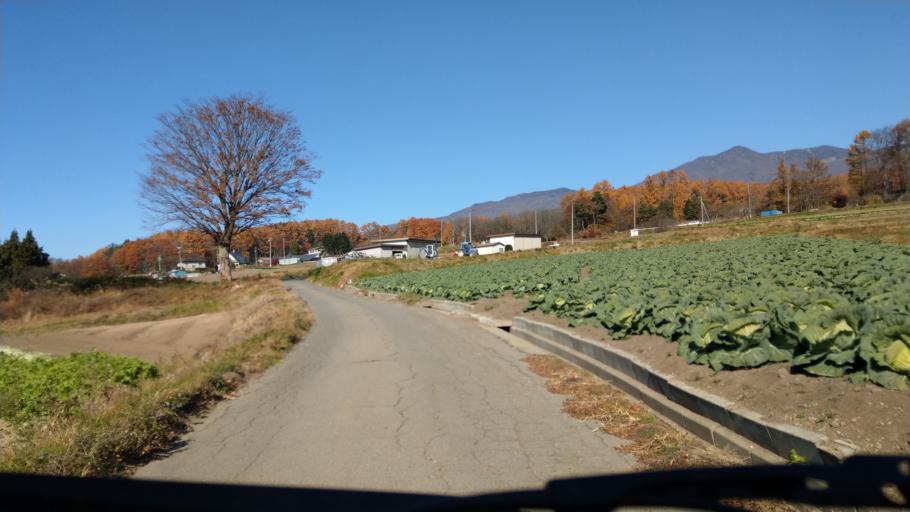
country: JP
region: Nagano
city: Komoro
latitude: 36.3370
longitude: 138.4578
